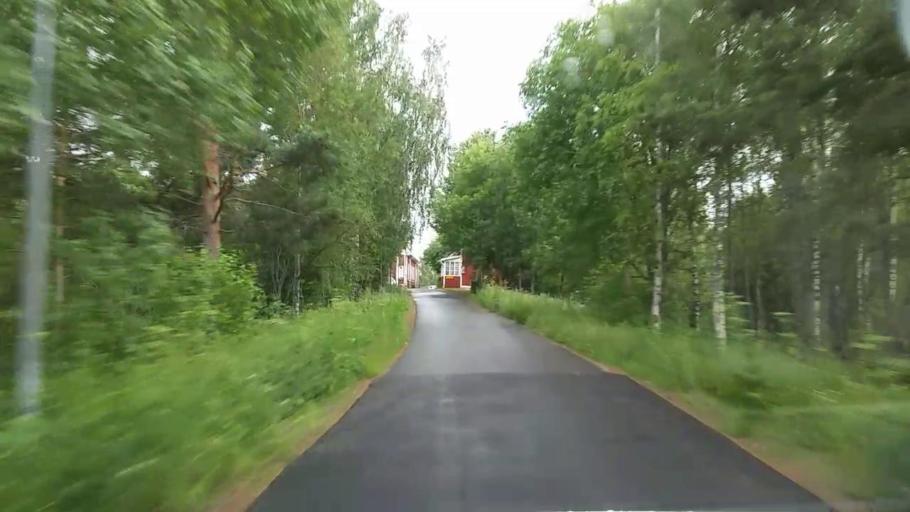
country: SE
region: Gaevleborg
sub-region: Ljusdals Kommun
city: Jaervsoe
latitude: 61.7155
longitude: 16.1775
